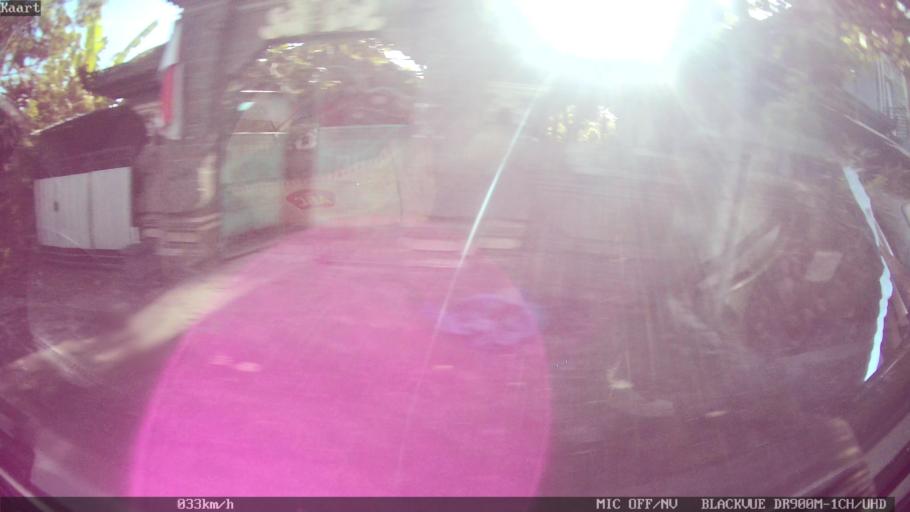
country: ID
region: Bali
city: Banjar Sedang
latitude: -8.5710
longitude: 115.2376
